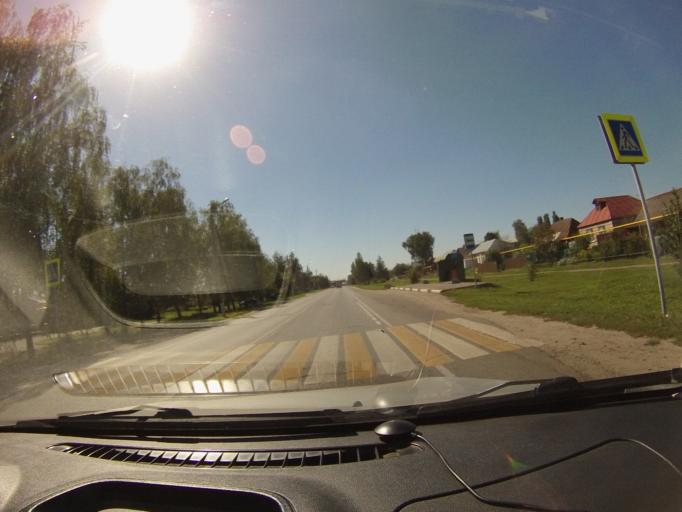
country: RU
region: Tambov
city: Donskoye
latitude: 52.7670
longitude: 41.4783
